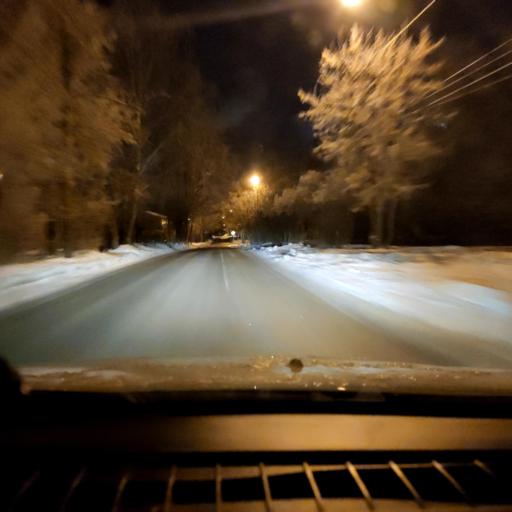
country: RU
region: Samara
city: Novosemeykino
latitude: 53.3417
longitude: 50.2283
